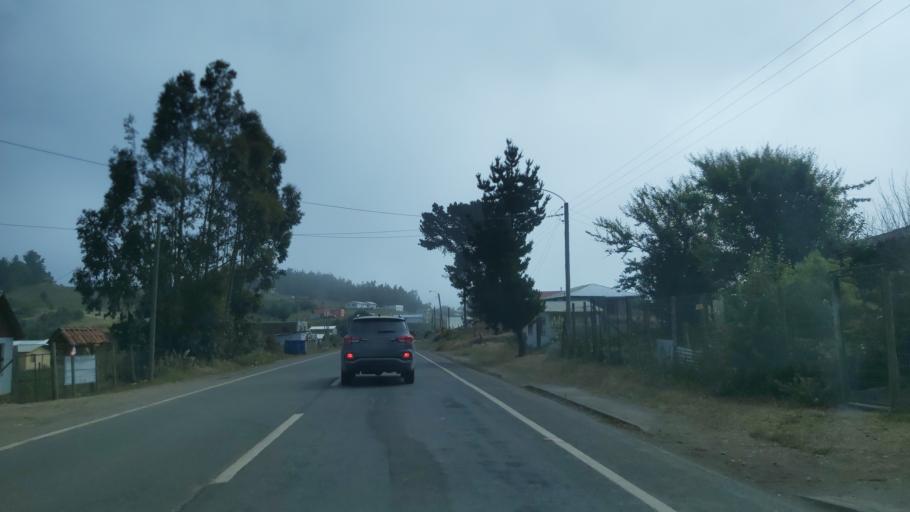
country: CL
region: Maule
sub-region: Provincia de Cauquenes
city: Cauquenes
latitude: -35.8730
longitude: -72.6617
